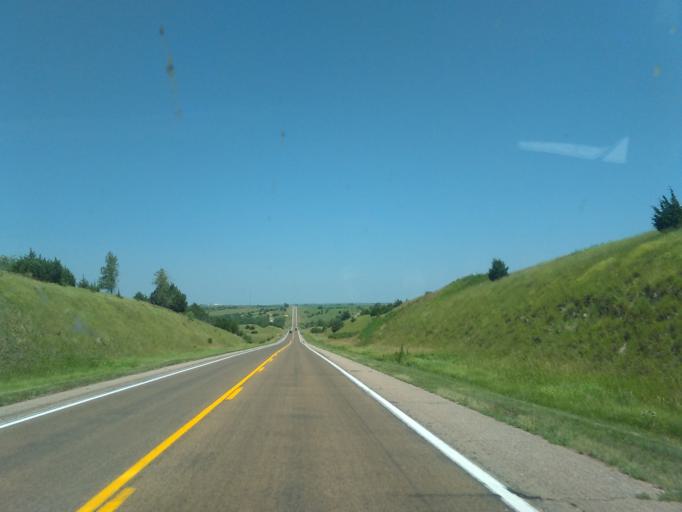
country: US
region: Nebraska
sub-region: Frontier County
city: Stockville
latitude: 40.6202
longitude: -100.6304
